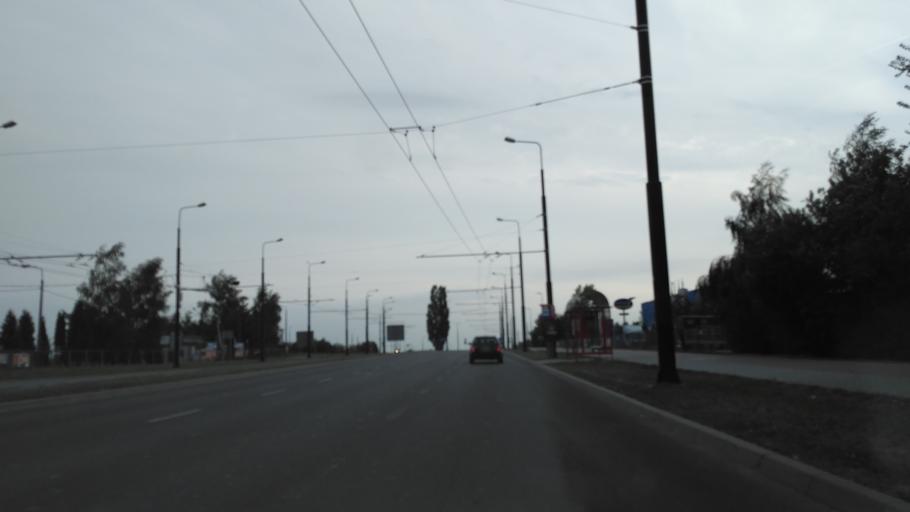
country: PL
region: Lublin Voivodeship
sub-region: Powiat lubelski
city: Jakubowice Murowane
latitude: 51.2305
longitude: 22.6219
